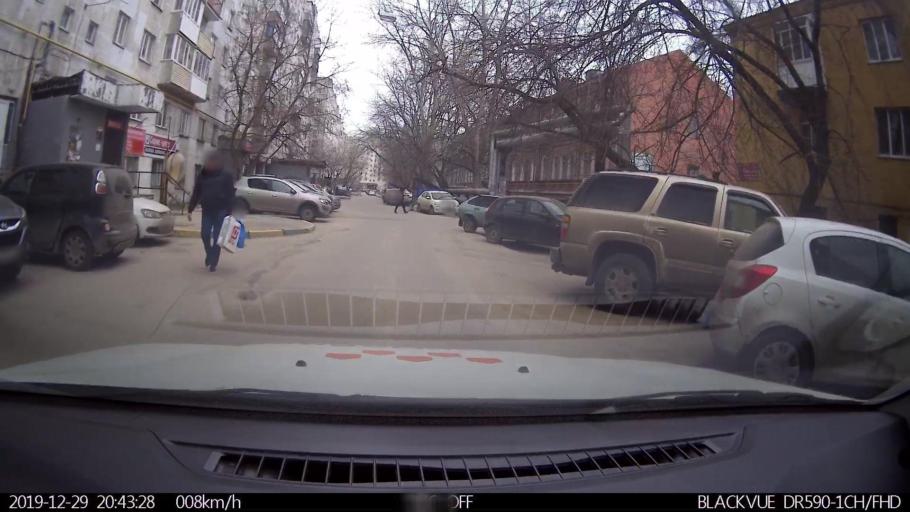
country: RU
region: Nizjnij Novgorod
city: Nizhniy Novgorod
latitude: 56.3280
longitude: 43.9534
